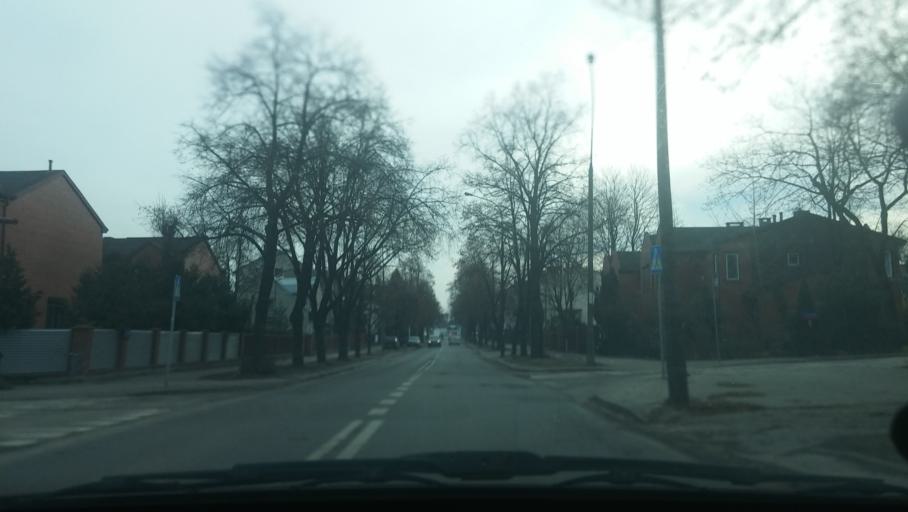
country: PL
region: Masovian Voivodeship
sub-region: Warszawa
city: Targowek
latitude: 52.2781
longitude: 21.0632
